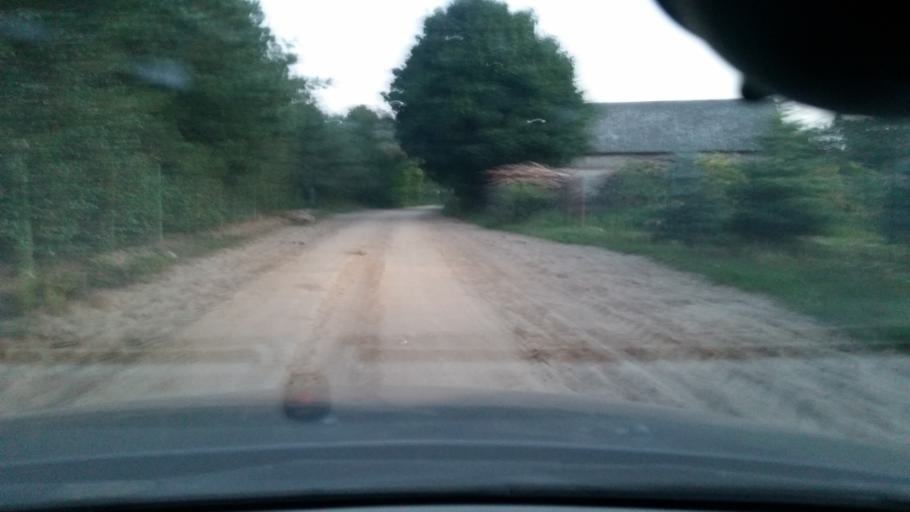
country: PL
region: Pomeranian Voivodeship
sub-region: Powiat wejherowski
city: Choczewo
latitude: 54.7711
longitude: 17.7959
